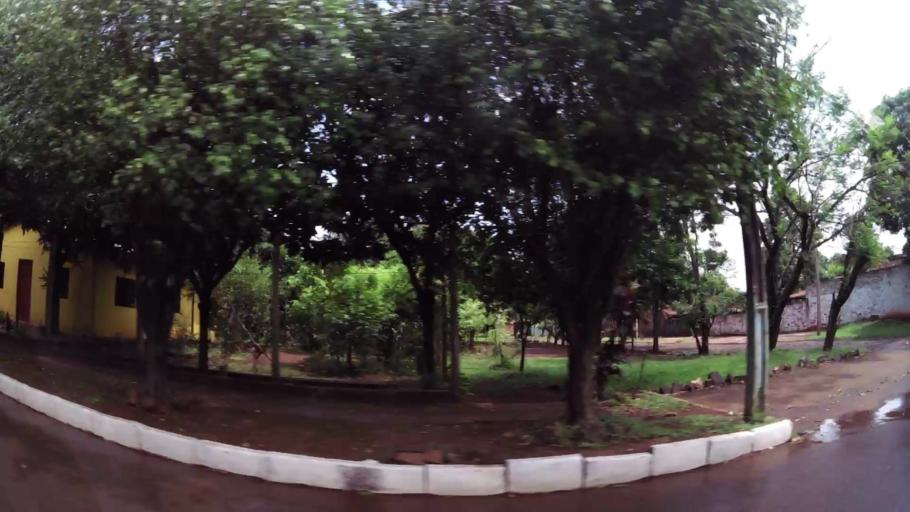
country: PY
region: Alto Parana
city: Ciudad del Este
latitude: -25.5045
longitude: -54.6625
